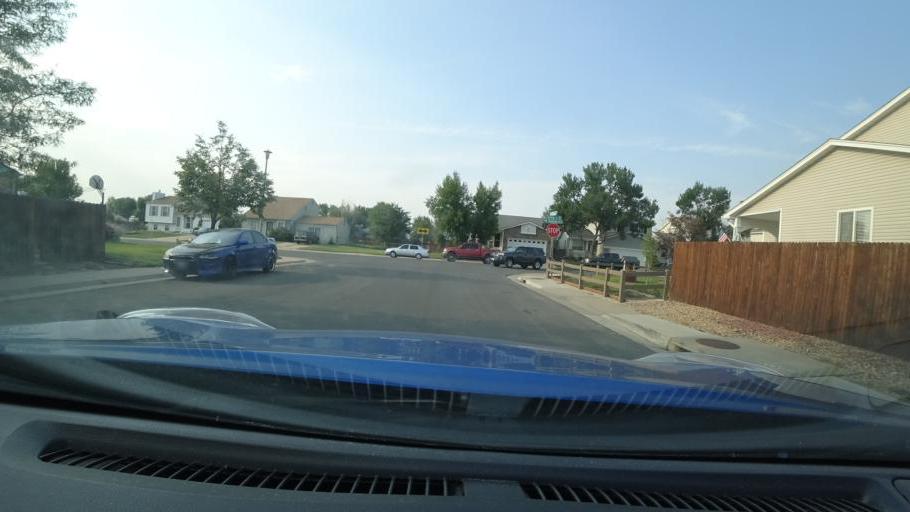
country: US
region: Colorado
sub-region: Adams County
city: Aurora
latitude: 39.7466
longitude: -104.7630
